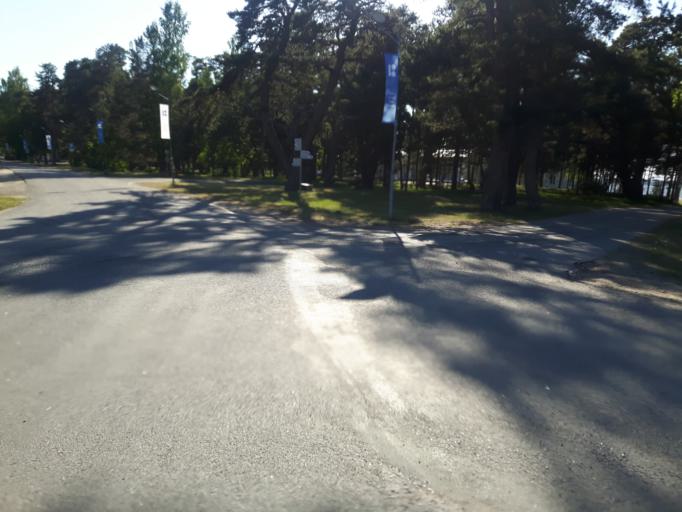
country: EE
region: Harju
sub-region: Loksa linn
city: Loksa
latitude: 59.5791
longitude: 25.9689
